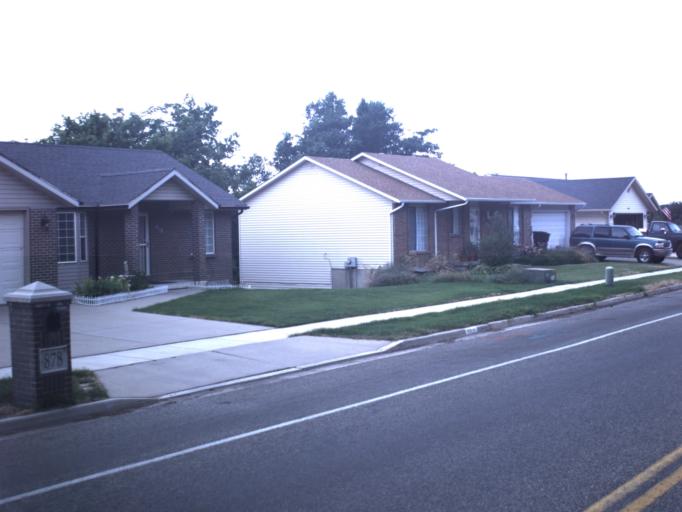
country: US
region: Utah
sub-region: Davis County
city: Farmington
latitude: 40.9658
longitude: -111.8834
